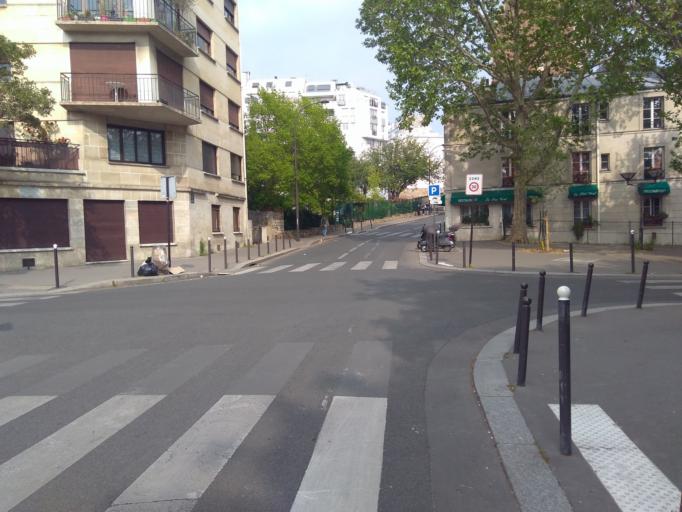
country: FR
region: Ile-de-France
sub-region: Departement du Val-de-Marne
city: Le Kremlin-Bicetre
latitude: 48.8268
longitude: 2.3533
